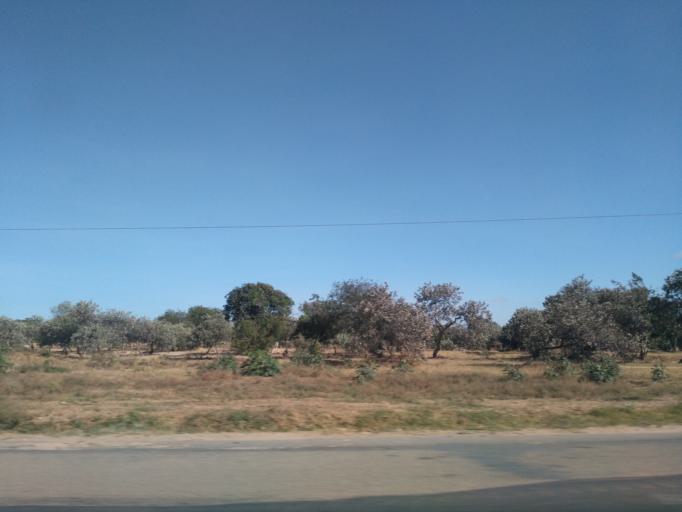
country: TZ
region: Dodoma
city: Dodoma
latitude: -6.1781
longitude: 35.7357
